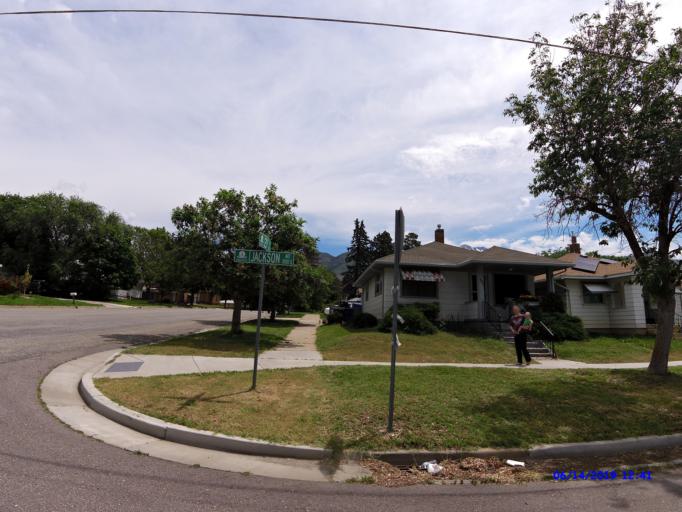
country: US
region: Utah
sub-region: Weber County
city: Ogden
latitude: 41.2287
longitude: -111.9535
